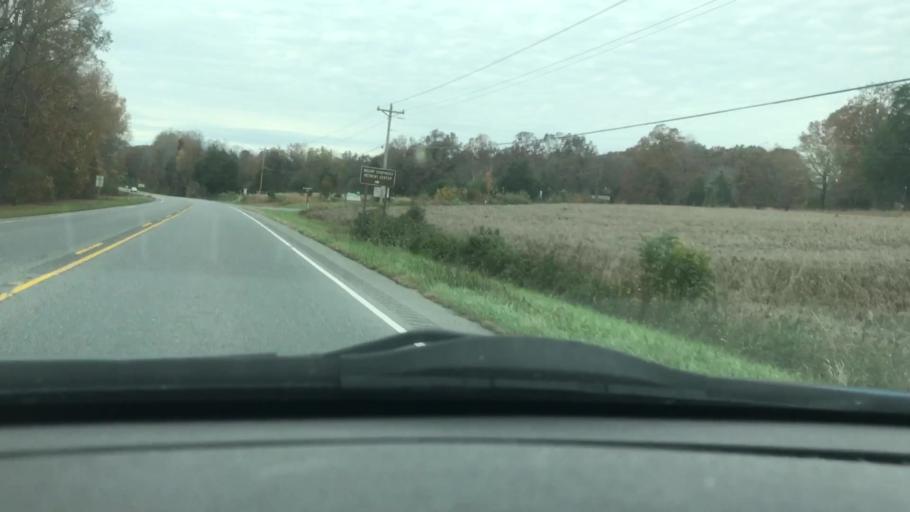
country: US
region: North Carolina
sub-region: Randolph County
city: Asheboro
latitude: 35.7310
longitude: -79.9434
